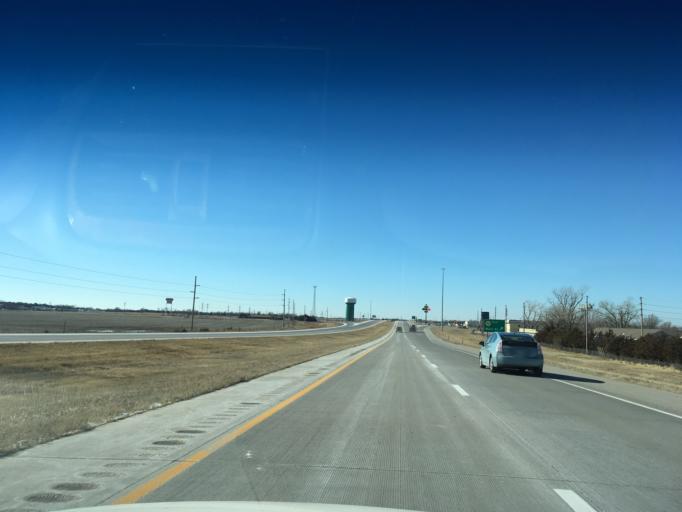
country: US
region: Kansas
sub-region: Reno County
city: South Hutchinson
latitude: 38.0133
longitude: -97.9333
